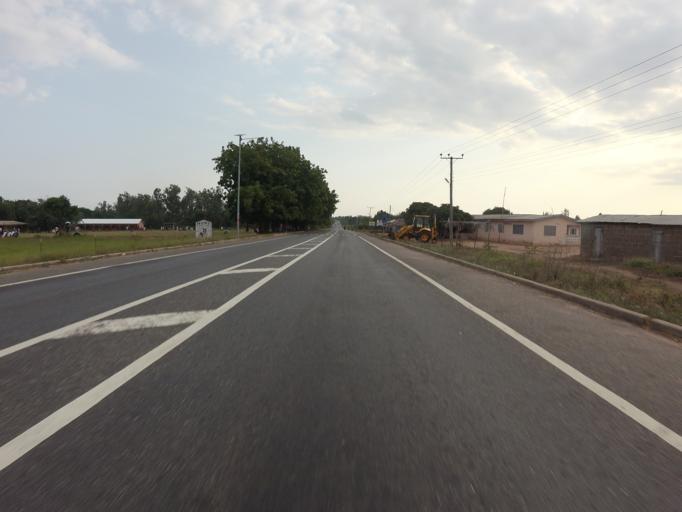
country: GH
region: Volta
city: Anloga
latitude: 6.1032
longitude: 0.5132
